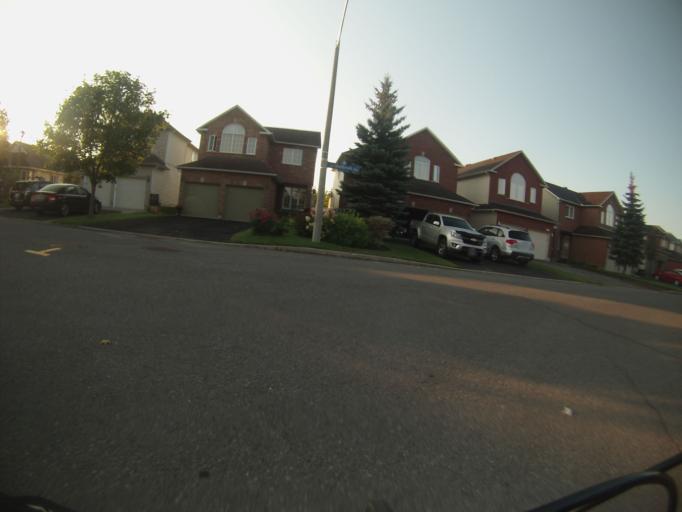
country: CA
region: Ontario
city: Ottawa
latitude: 45.3698
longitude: -75.6298
